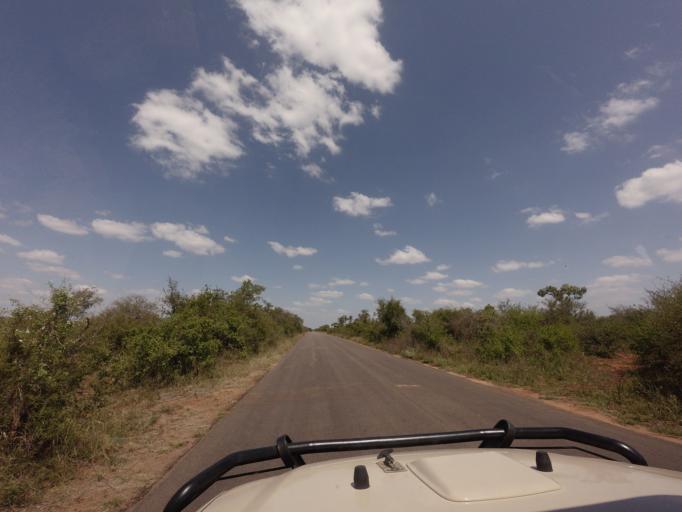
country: ZA
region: Mpumalanga
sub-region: Ehlanzeni District
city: Komatipoort
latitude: -25.1030
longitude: 31.8966
